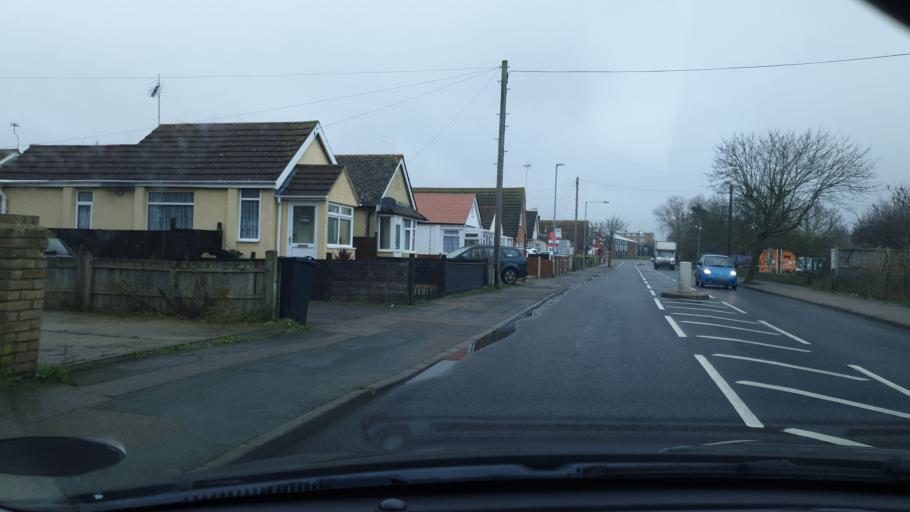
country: GB
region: England
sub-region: Essex
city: Clacton-on-Sea
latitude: 51.7798
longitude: 1.1204
